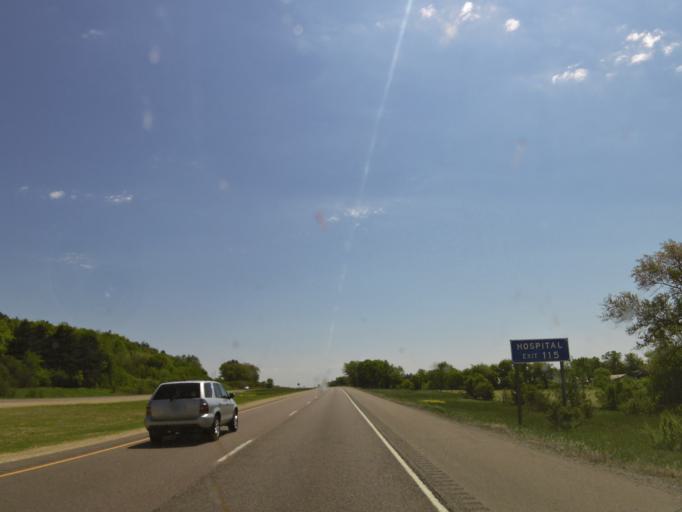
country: US
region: Wisconsin
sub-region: Jackson County
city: Black River Falls
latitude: 44.3125
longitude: -90.8573
